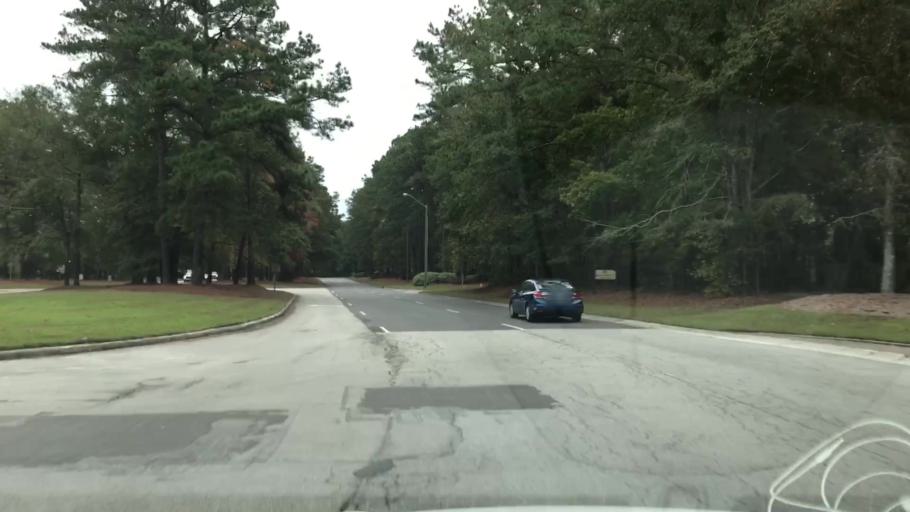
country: US
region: South Carolina
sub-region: Berkeley County
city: Goose Creek
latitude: 33.0079
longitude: -80.0545
